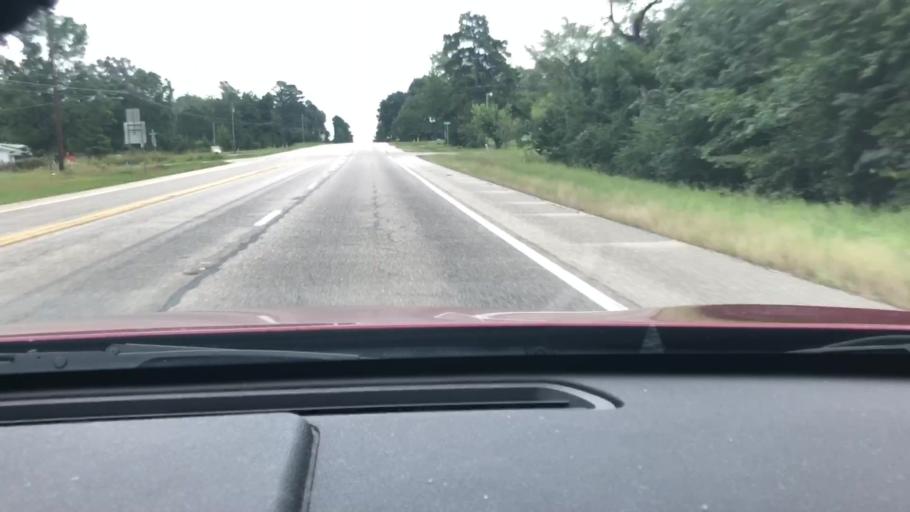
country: US
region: Arkansas
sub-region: Miller County
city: Texarkana
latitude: 33.4294
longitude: -93.9439
